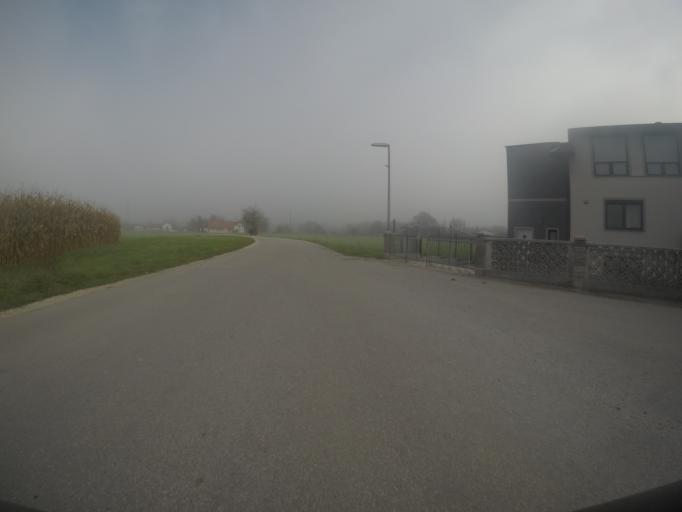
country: SI
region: Domzale
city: Dob
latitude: 46.1563
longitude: 14.6291
